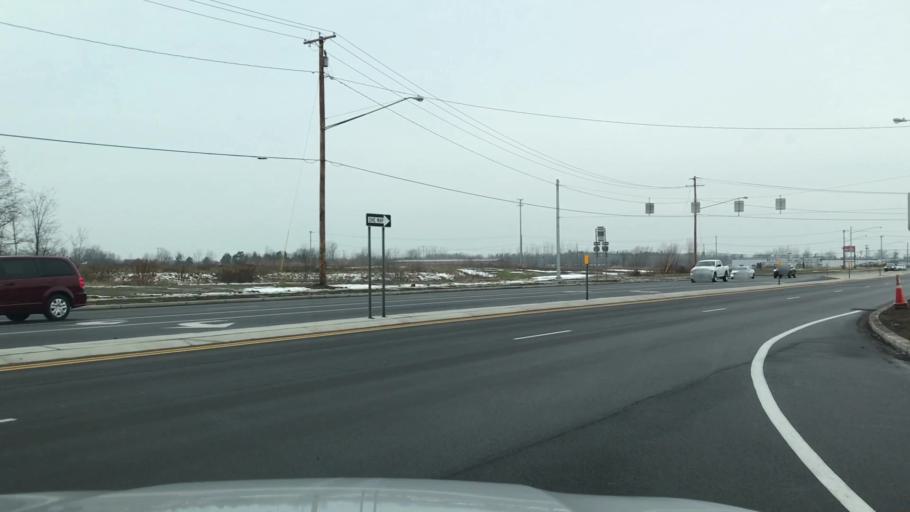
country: US
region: New York
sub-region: Erie County
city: Hamburg
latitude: 42.7433
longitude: -78.8489
